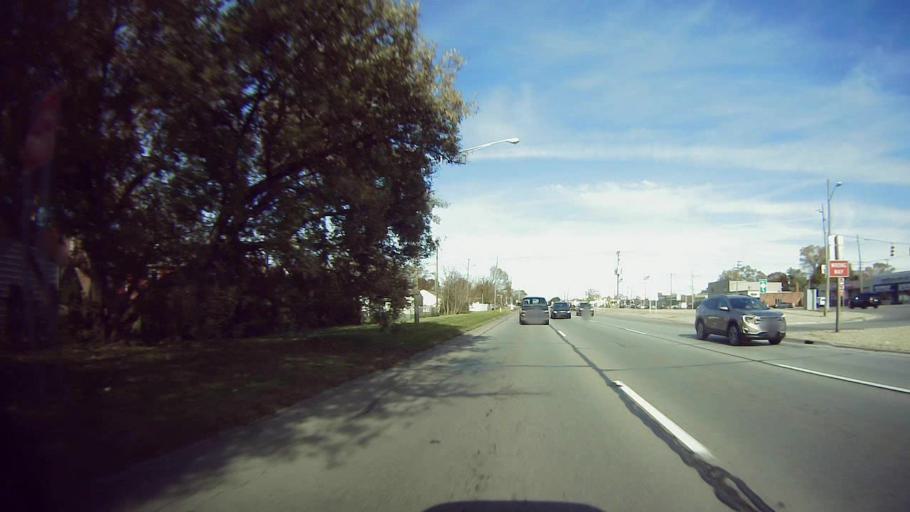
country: US
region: Michigan
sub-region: Wayne County
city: Dearborn Heights
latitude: 42.3245
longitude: -83.2728
